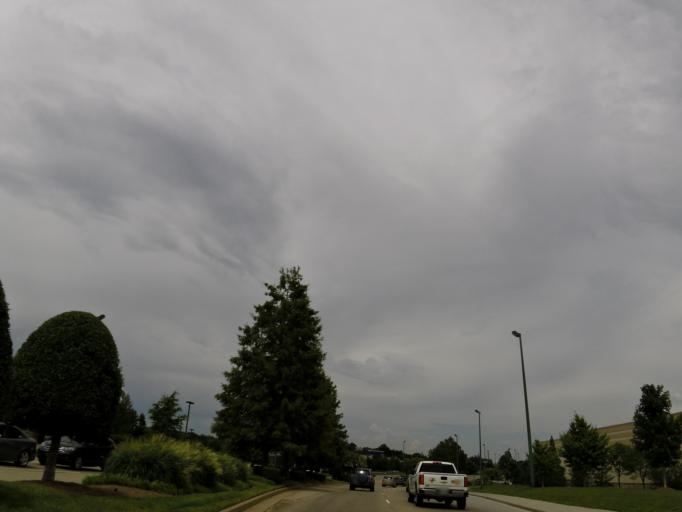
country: US
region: Tennessee
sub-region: Knox County
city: Farragut
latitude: 35.8971
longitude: -84.1697
